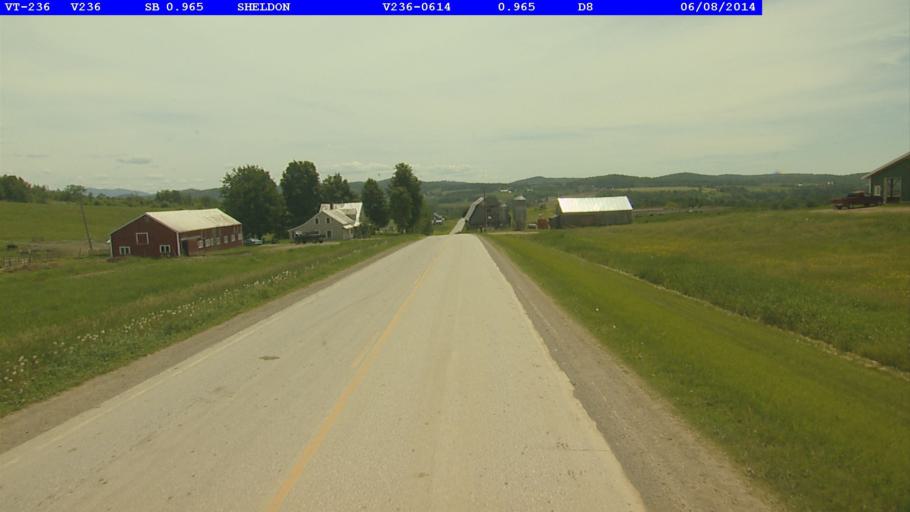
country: US
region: Vermont
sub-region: Franklin County
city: Enosburg Falls
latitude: 44.9248
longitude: -72.8656
